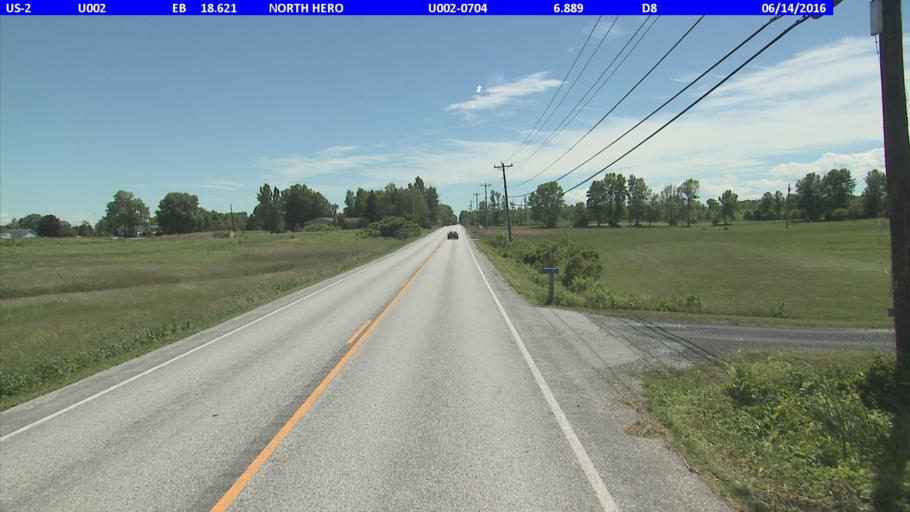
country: US
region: Vermont
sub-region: Grand Isle County
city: North Hero
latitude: 44.8003
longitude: -73.2921
